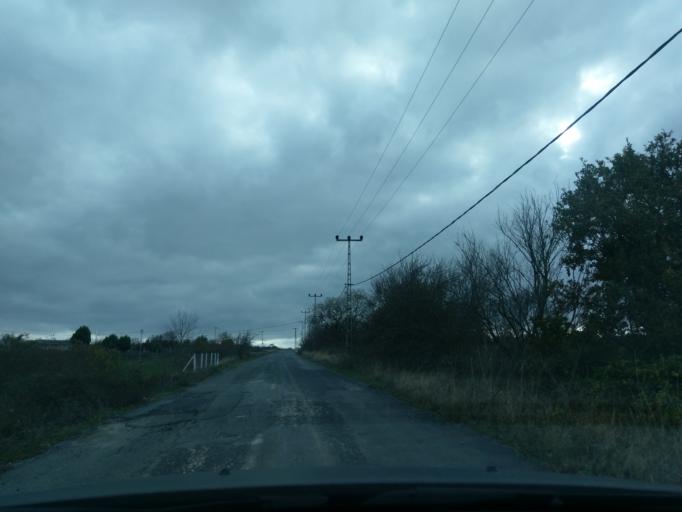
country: TR
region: Istanbul
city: Durusu
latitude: 41.2878
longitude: 28.6898
